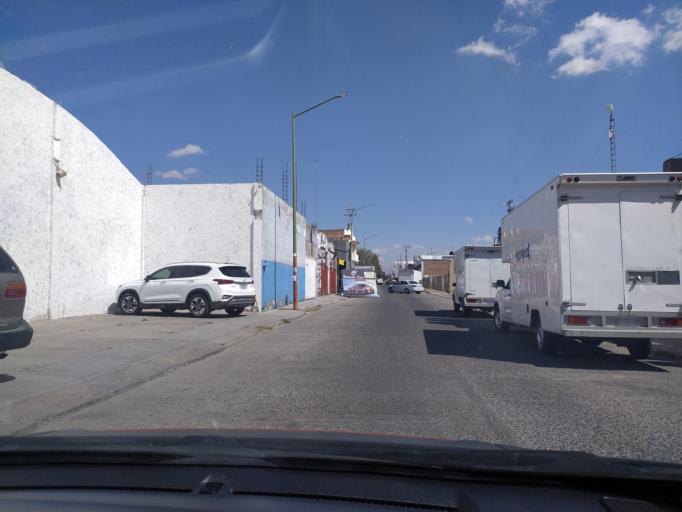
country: LA
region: Oudomxai
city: Muang La
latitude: 21.0241
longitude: 101.8542
